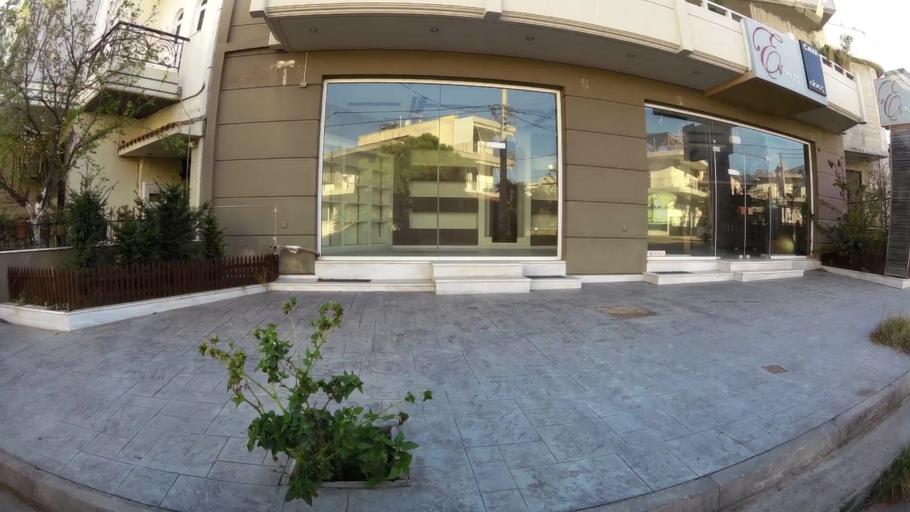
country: GR
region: Attica
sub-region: Nomarchia Anatolikis Attikis
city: Acharnes
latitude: 38.0859
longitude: 23.7239
